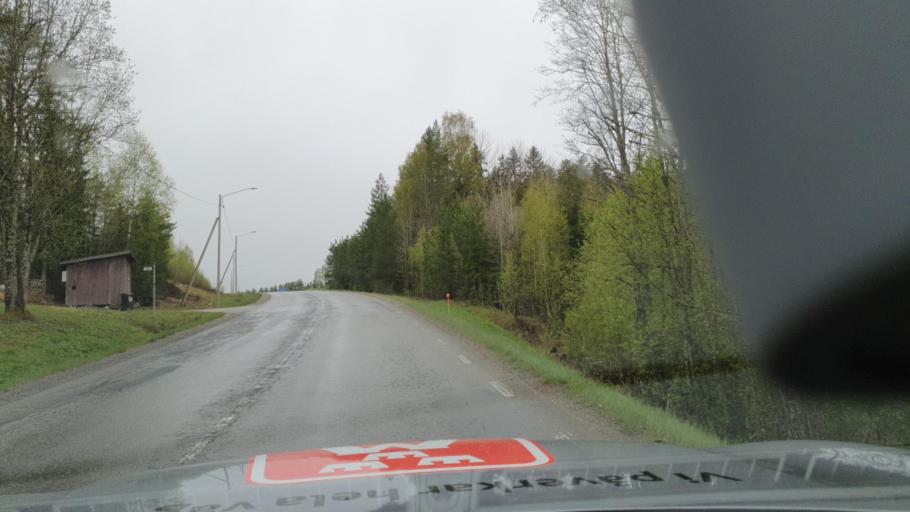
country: SE
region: Vaesternorrland
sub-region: OErnskoeldsviks Kommun
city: Bredbyn
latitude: 63.4695
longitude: 17.9615
